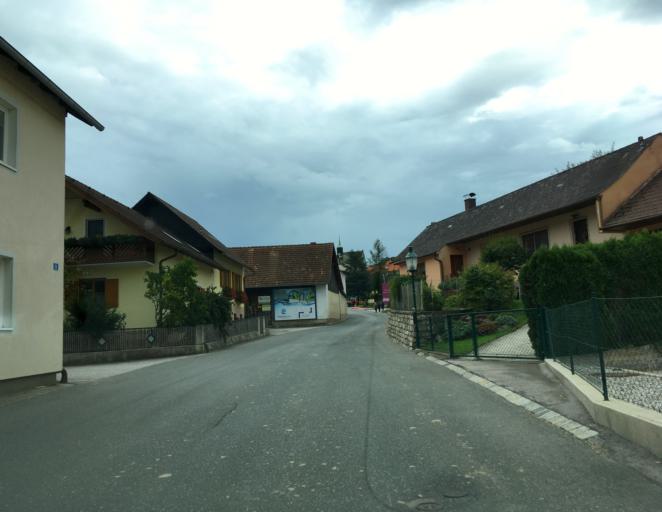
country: AT
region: Lower Austria
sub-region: Politischer Bezirk Wiener Neustadt
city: Bad Schonau
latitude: 47.4972
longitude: 16.2338
